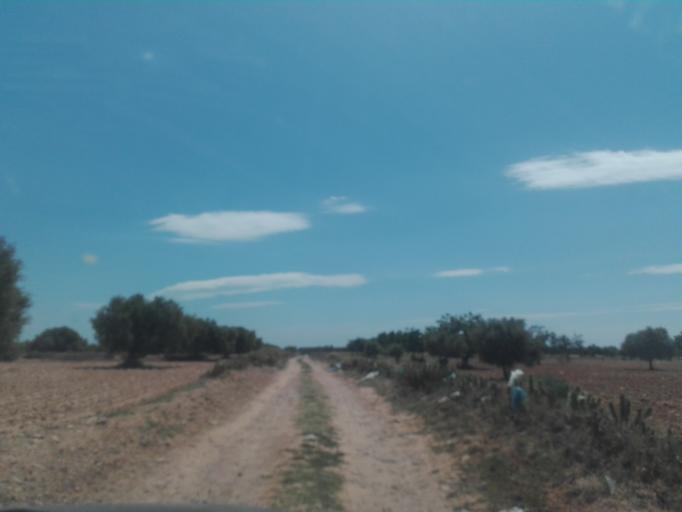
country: TN
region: Safaqis
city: Sfax
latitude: 34.6539
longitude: 10.5883
